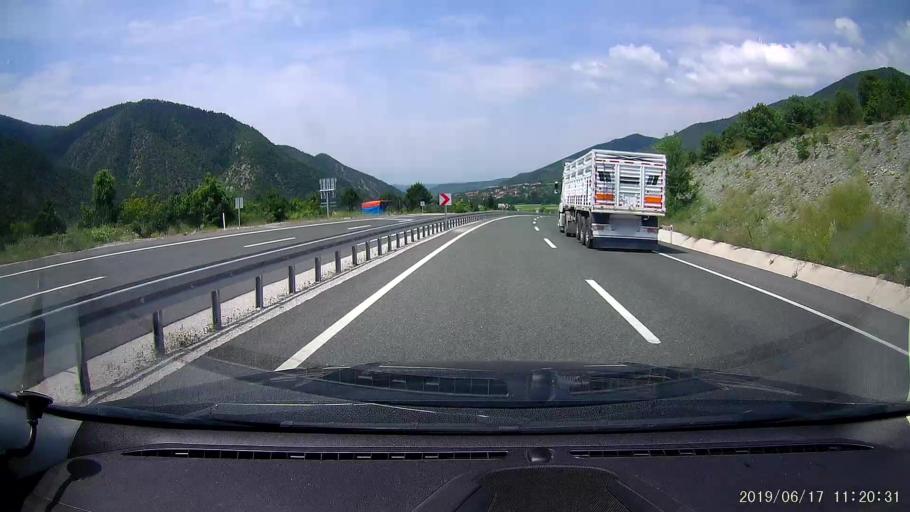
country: TR
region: Cankiri
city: Yaprakli
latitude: 40.9115
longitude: 33.8057
